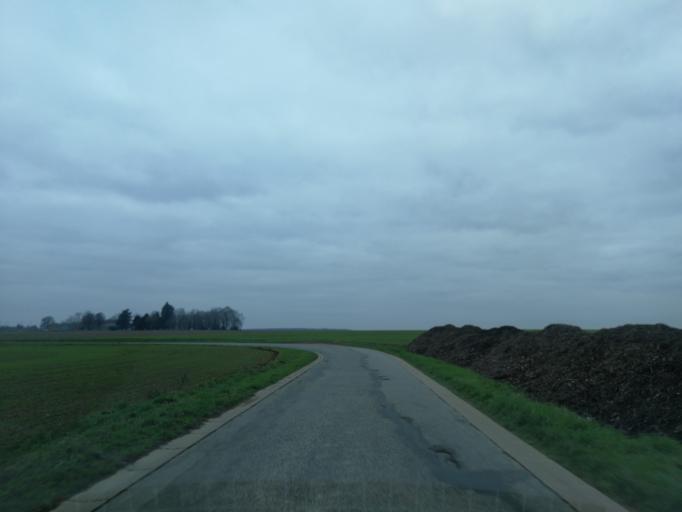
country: FR
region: Ile-de-France
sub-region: Departement de l'Essonne
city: Limours
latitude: 48.6636
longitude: 2.0917
